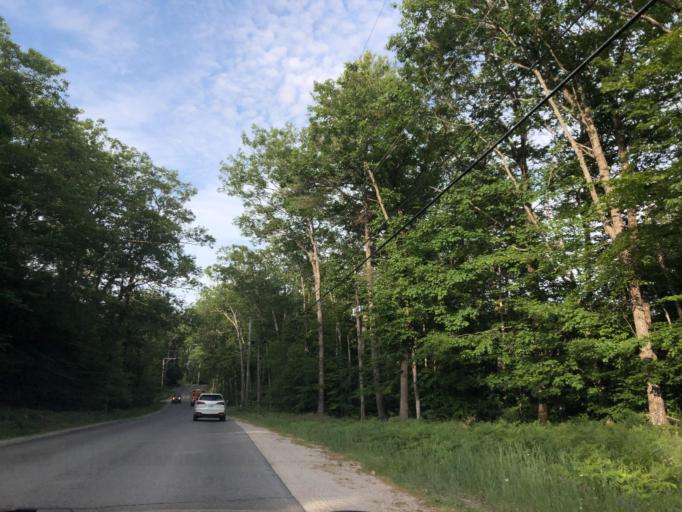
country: US
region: New Hampshire
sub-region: Merrimack County
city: Sutton
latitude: 43.3522
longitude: -71.9254
